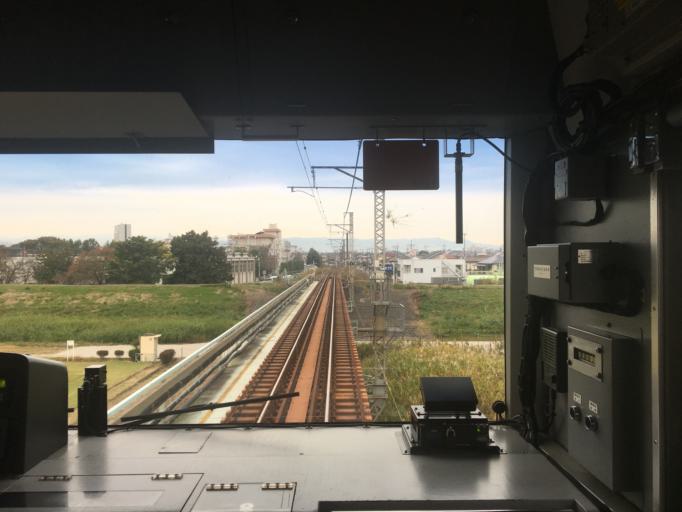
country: JP
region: Saitama
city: Kawagoe
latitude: 35.9205
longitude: 139.4523
